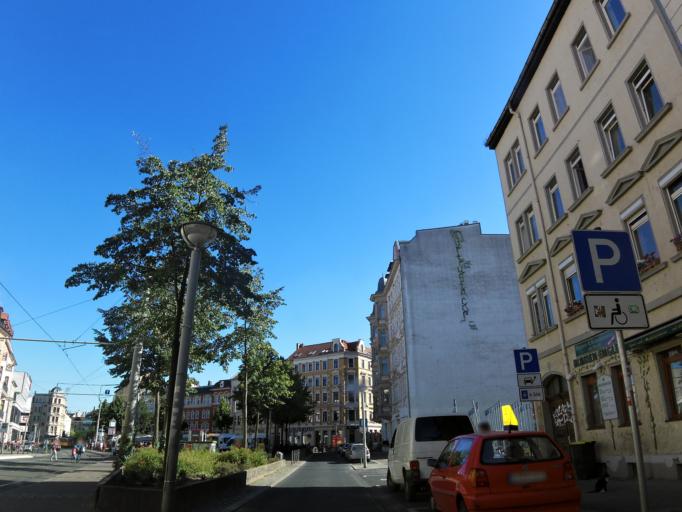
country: DE
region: Saxony
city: Leipzig
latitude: 51.3376
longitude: 12.3336
